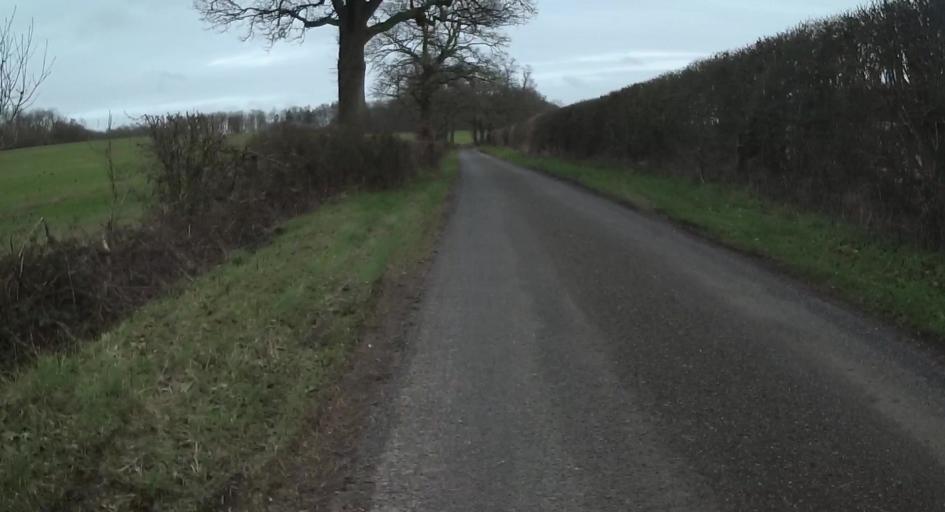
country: GB
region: England
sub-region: Hampshire
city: Overton
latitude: 51.2677
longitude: -1.2490
